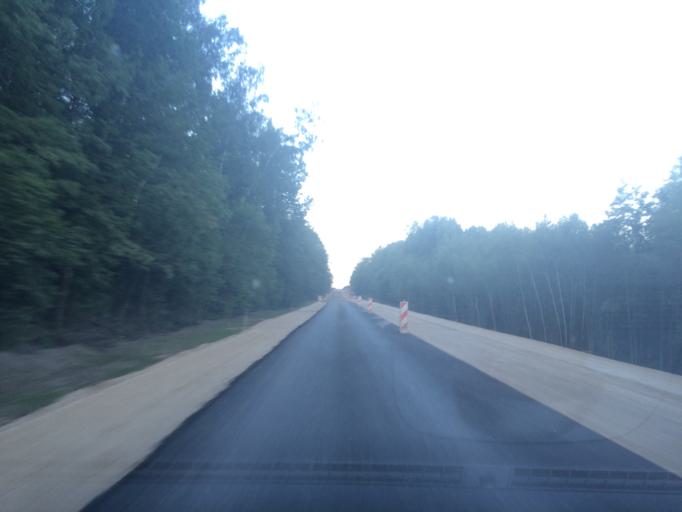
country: LT
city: Zarasai
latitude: 55.7591
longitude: 26.3299
